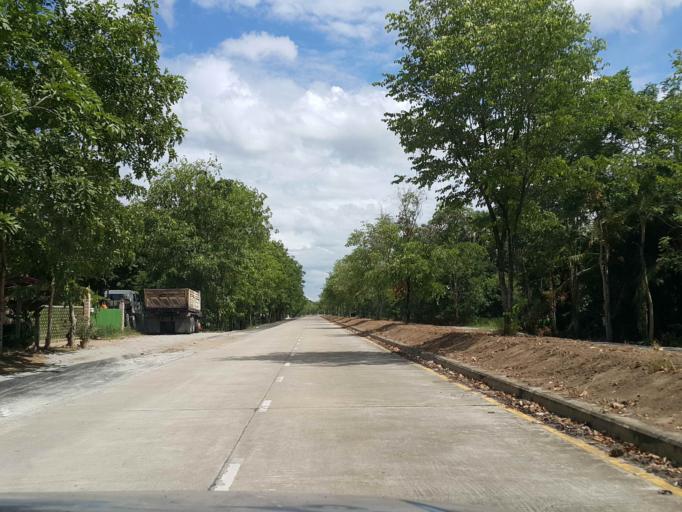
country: TH
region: Tak
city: Tak
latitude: 16.8765
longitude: 99.1109
